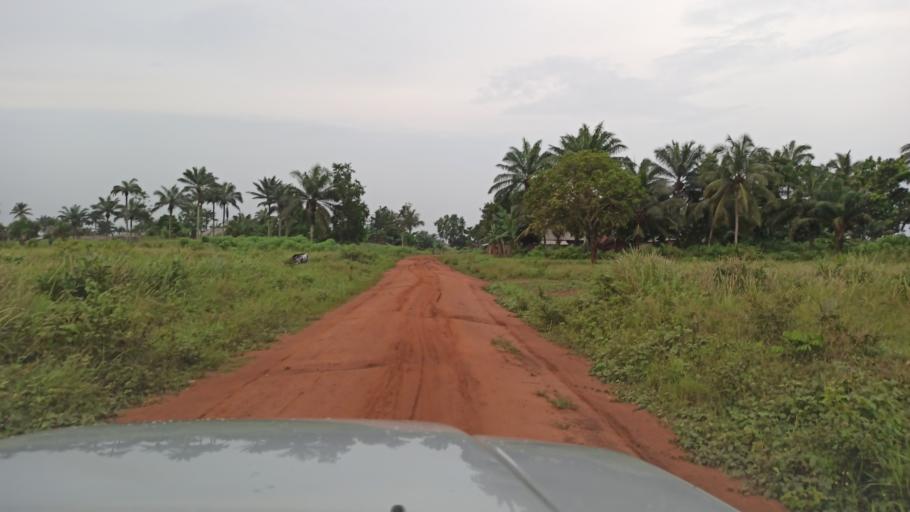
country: BJ
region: Queme
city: Porto-Novo
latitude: 6.4707
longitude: 2.6726
